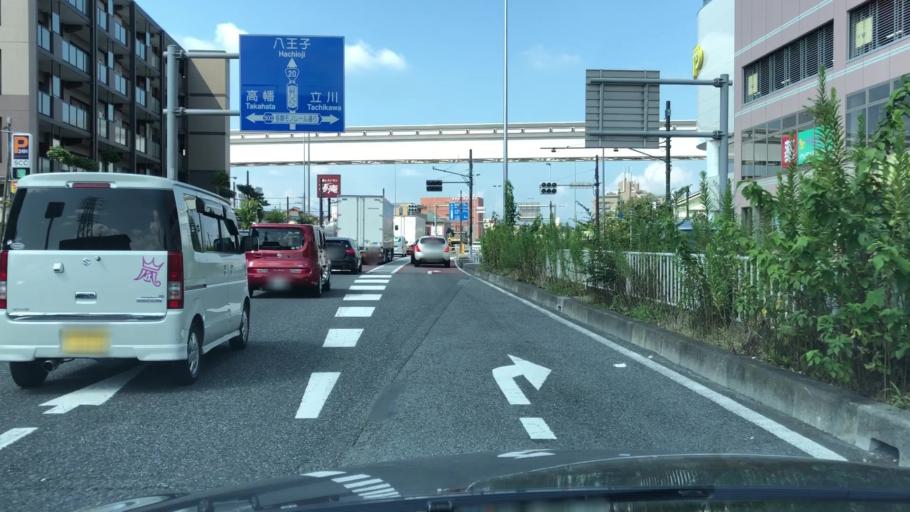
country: JP
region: Tokyo
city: Hino
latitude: 35.6708
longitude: 139.4214
